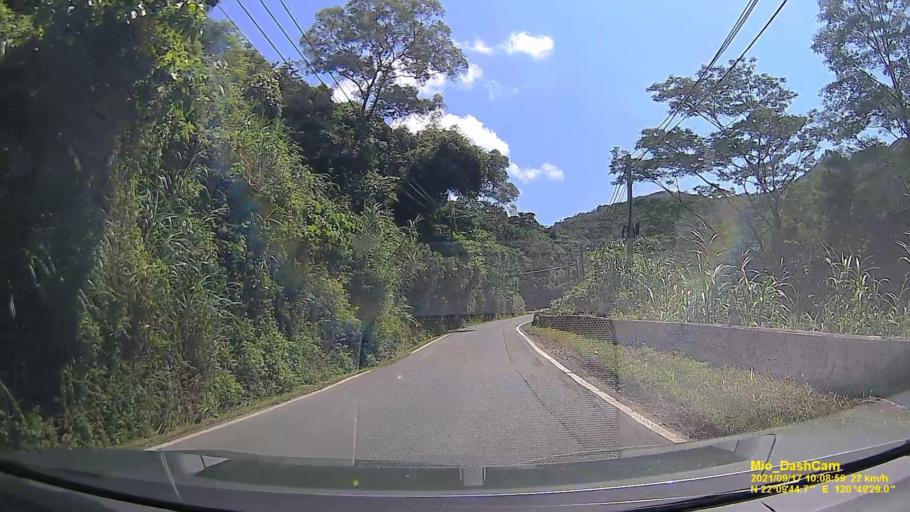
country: TW
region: Taiwan
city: Hengchun
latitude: 22.1624
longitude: 120.8248
